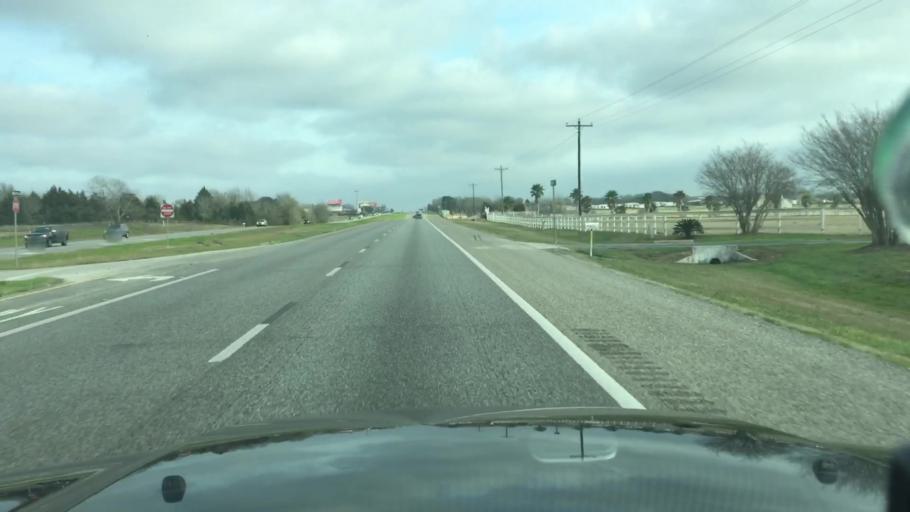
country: US
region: Texas
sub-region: Waller County
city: Hempstead
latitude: 30.1247
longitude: -96.1189
